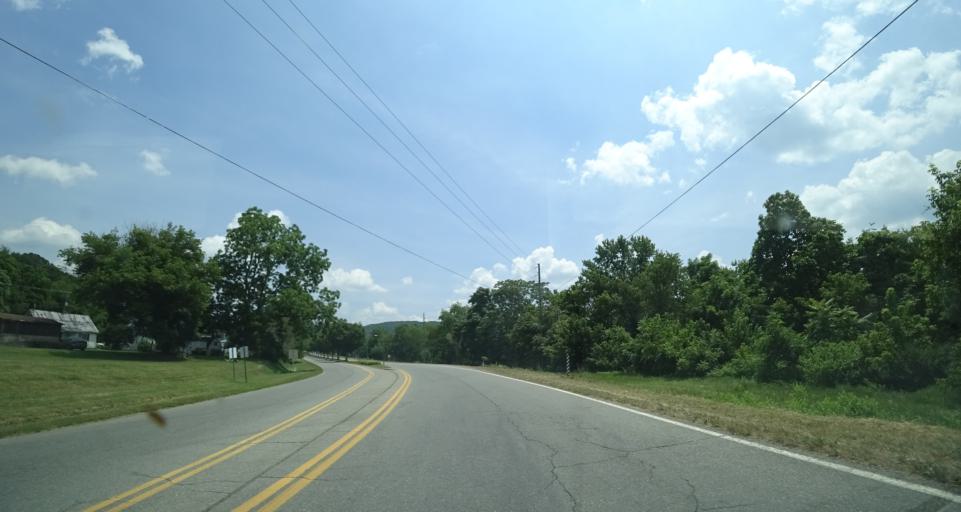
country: US
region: Virginia
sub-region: City of Radford
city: Radford
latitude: 37.1084
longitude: -80.5892
